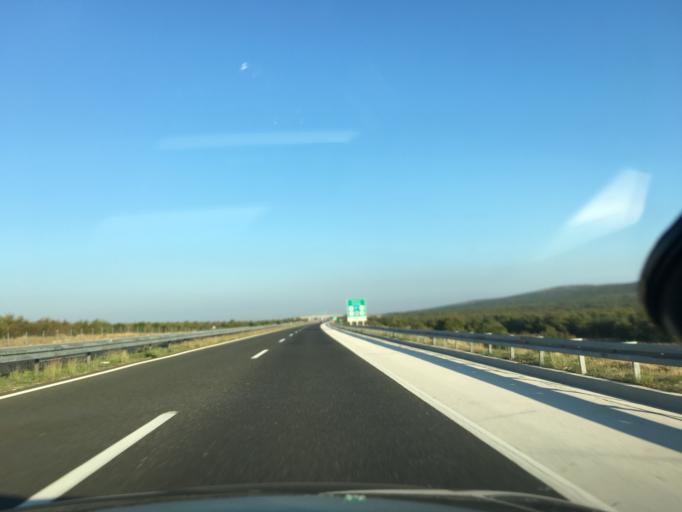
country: HR
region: Sibensko-Kniniska
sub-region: Grad Sibenik
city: Pirovac
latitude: 43.9359
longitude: 15.7075
